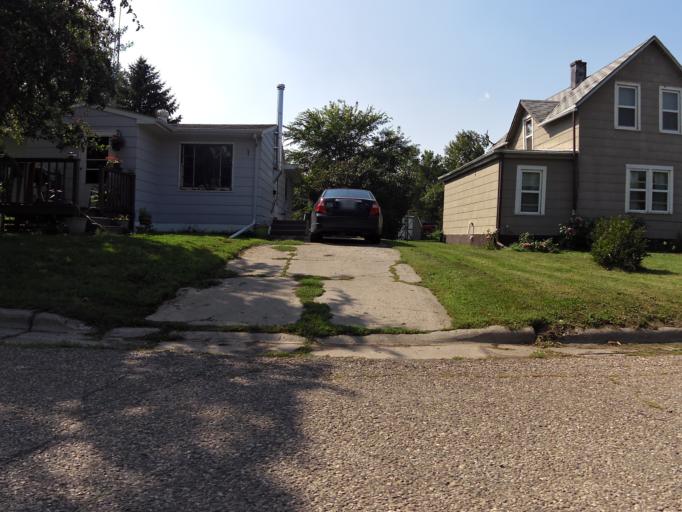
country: US
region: North Dakota
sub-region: Walsh County
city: Grafton
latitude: 48.4163
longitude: -97.4011
